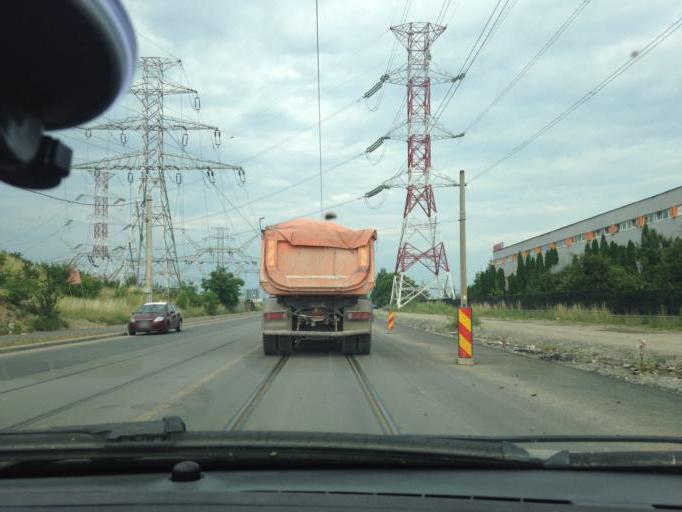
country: RO
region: Cluj
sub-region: Municipiul Cluj-Napoca
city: Cluj-Napoca
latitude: 46.7962
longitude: 23.6430
